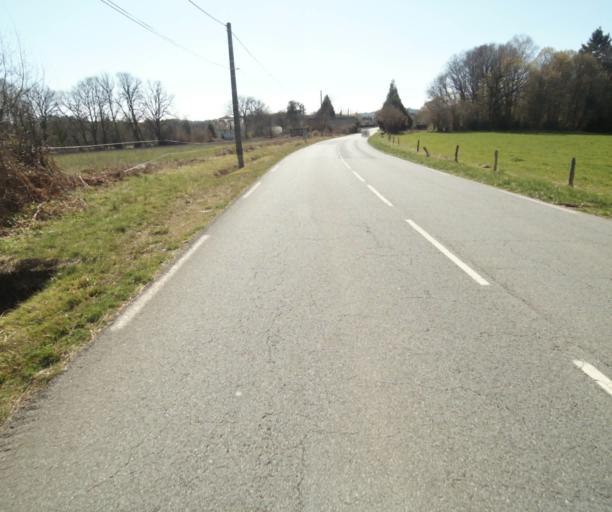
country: FR
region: Limousin
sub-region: Departement de la Correze
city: Saint-Mexant
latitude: 45.3040
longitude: 1.6774
